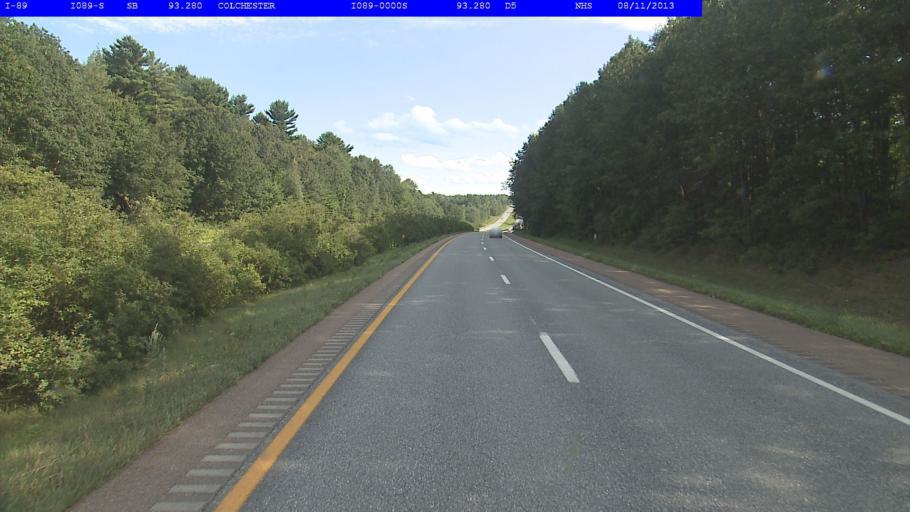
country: US
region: Vermont
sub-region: Chittenden County
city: Winooski
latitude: 44.5283
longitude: -73.1943
